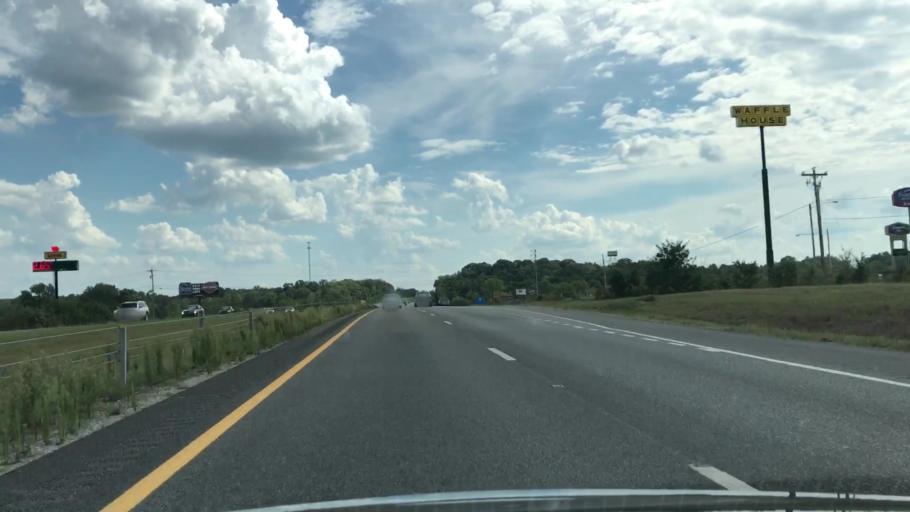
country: US
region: Tennessee
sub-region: Maury County
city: Spring Hill
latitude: 35.6462
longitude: -86.8936
